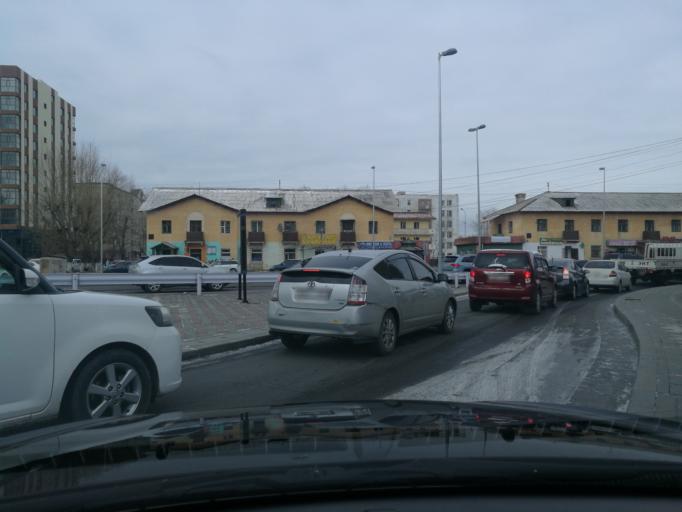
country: MN
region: Ulaanbaatar
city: Ulaanbaatar
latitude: 47.9109
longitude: 106.8953
